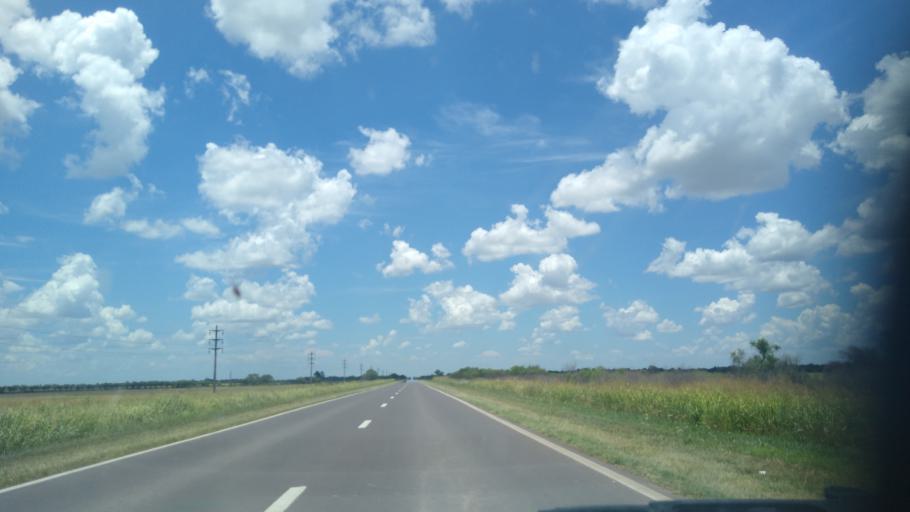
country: AR
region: Chaco
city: Presidencia Roque Saenz Pena
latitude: -26.7324
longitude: -60.3833
